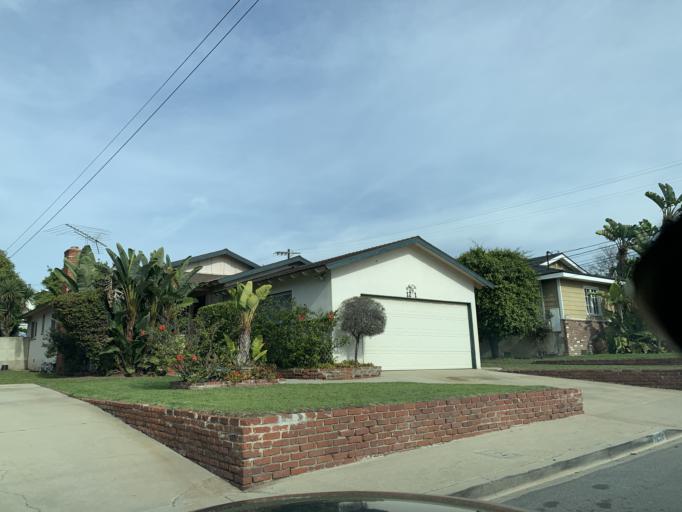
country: US
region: California
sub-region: Los Angeles County
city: Manhattan Beach
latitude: 33.8857
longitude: -118.3921
